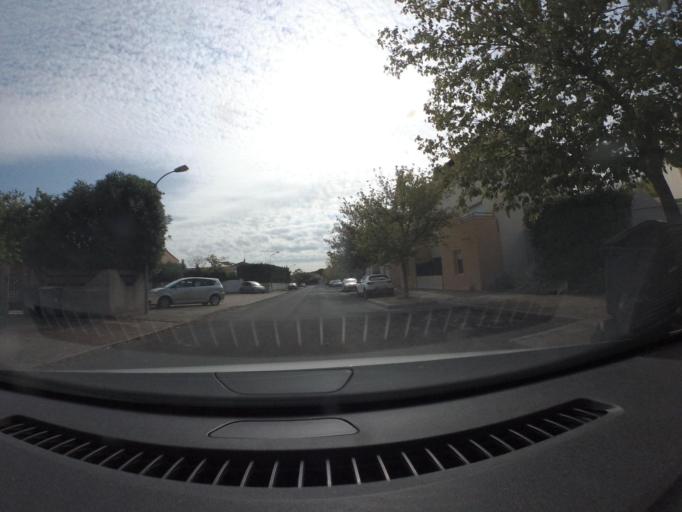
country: FR
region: Languedoc-Roussillon
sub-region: Departement de l'Herault
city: Baillargues
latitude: 43.6668
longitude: 4.0199
